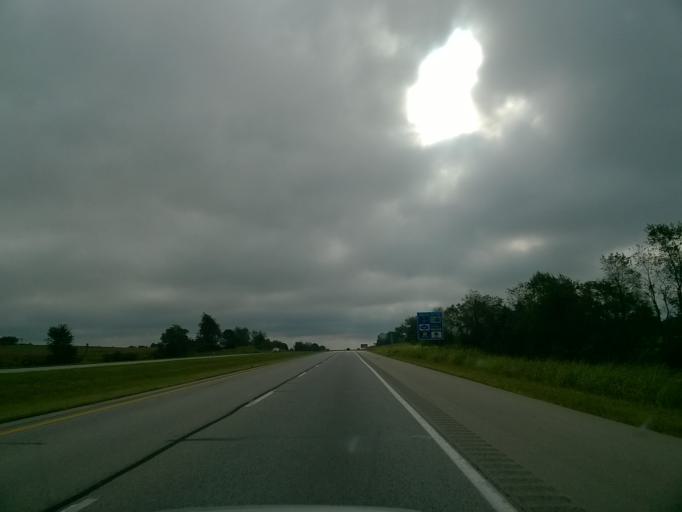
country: US
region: Indiana
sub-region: Harrison County
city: Corydon
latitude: 38.2412
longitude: -86.1646
